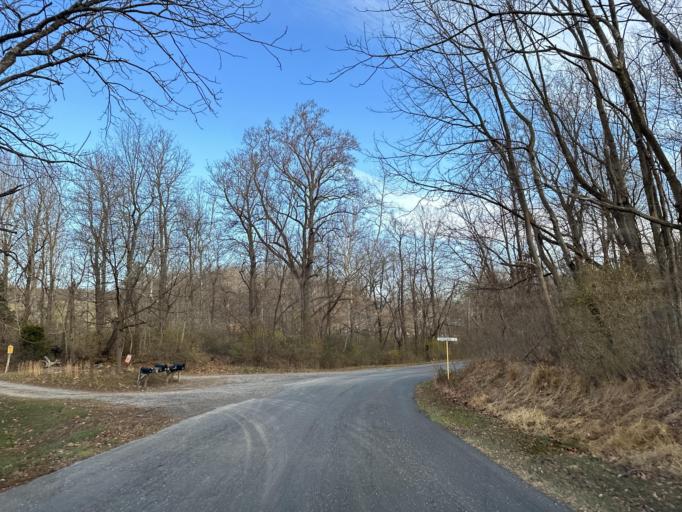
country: US
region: Virginia
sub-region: City of Staunton
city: Staunton
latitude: 38.2217
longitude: -79.2134
